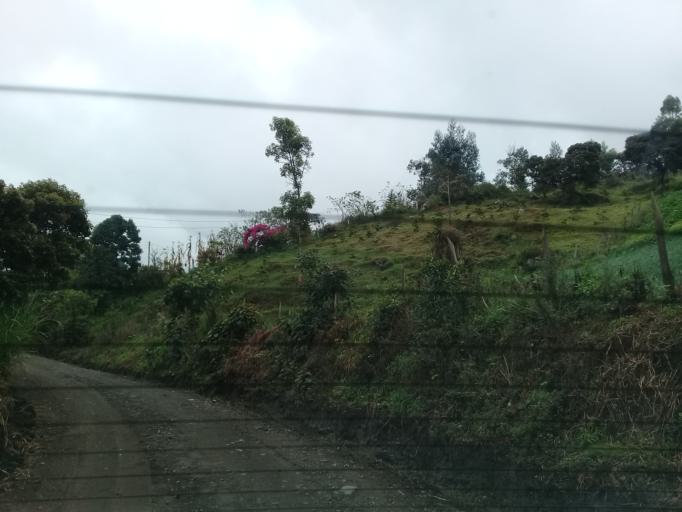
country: CO
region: Cundinamarca
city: Caqueza
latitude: 4.3994
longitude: -73.9854
